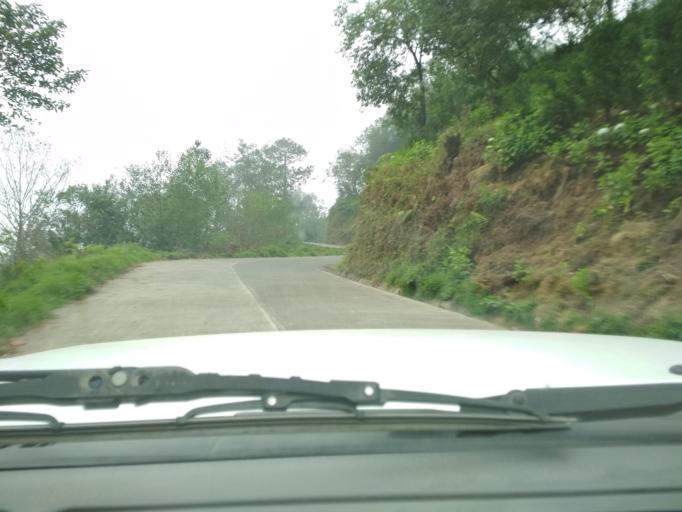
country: MX
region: Veracruz
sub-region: La Perla
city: Chilapa
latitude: 18.9741
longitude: -97.1656
